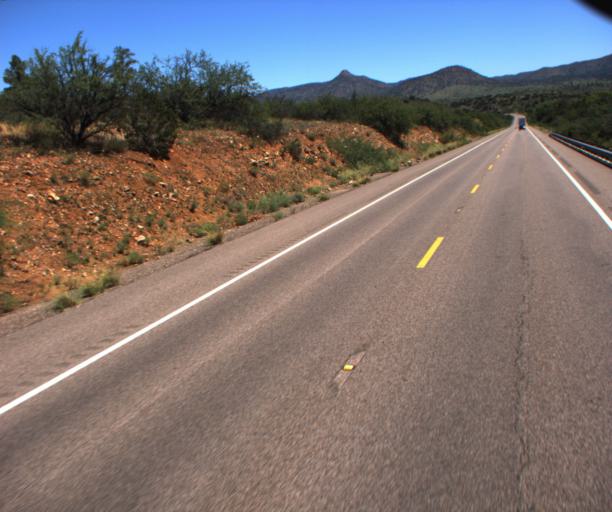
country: US
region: Arizona
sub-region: Gila County
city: Globe
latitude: 33.5718
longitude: -110.6613
